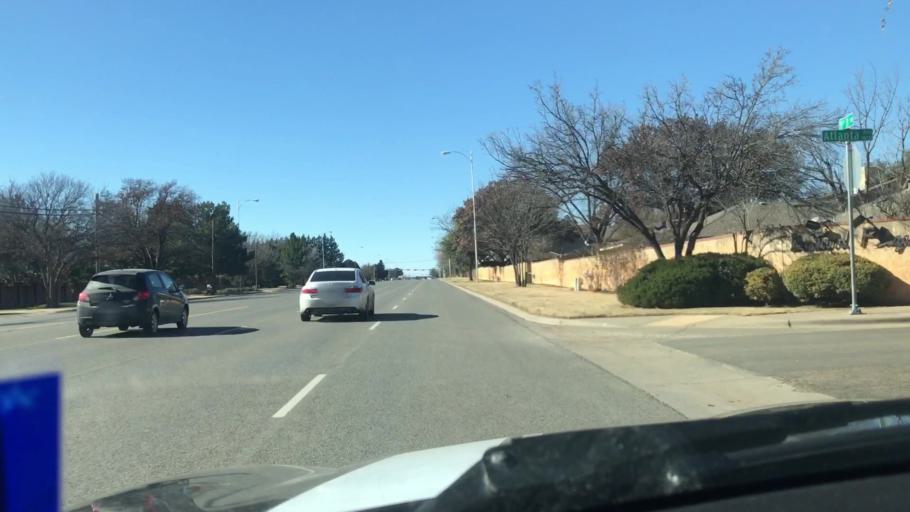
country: US
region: Texas
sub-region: Lubbock County
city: Lubbock
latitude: 33.5779
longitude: -101.9261
